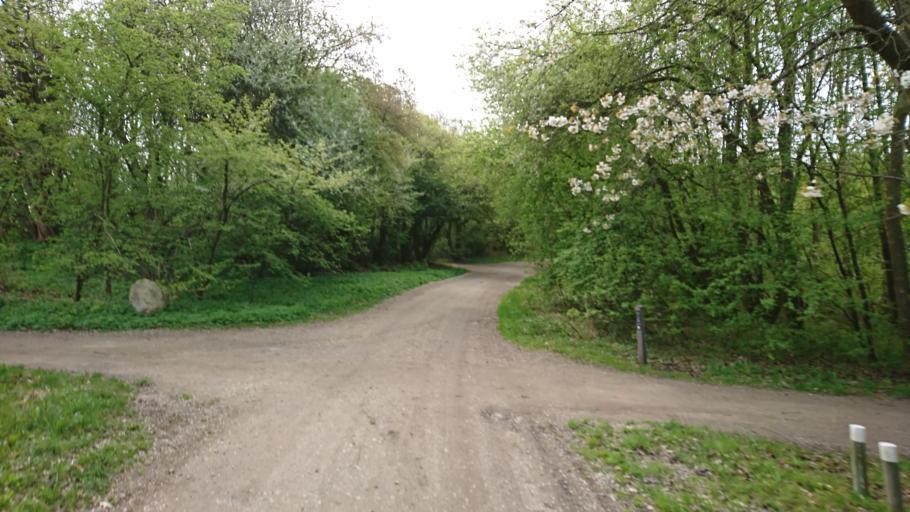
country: DK
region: Capital Region
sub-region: Ballerup Kommune
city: Ballerup
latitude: 55.7454
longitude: 12.3984
